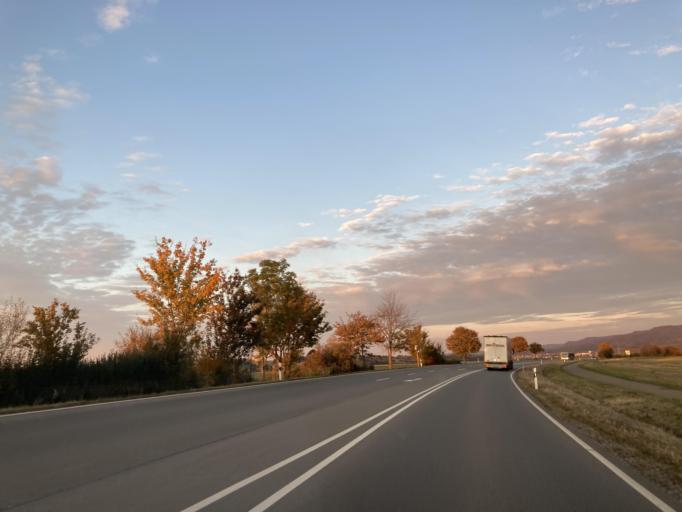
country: DE
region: Baden-Wuerttemberg
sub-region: Tuebingen Region
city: Dotternhausen
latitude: 48.2424
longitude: 8.8031
